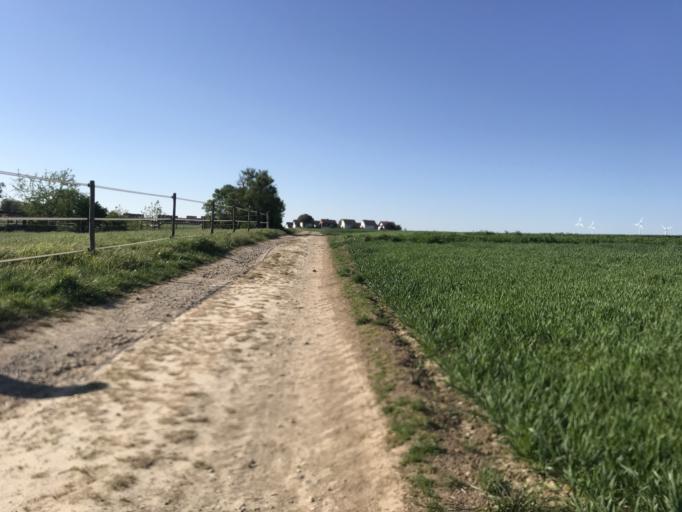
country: DE
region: Rheinland-Pfalz
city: Harxheim
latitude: 49.9201
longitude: 8.2408
